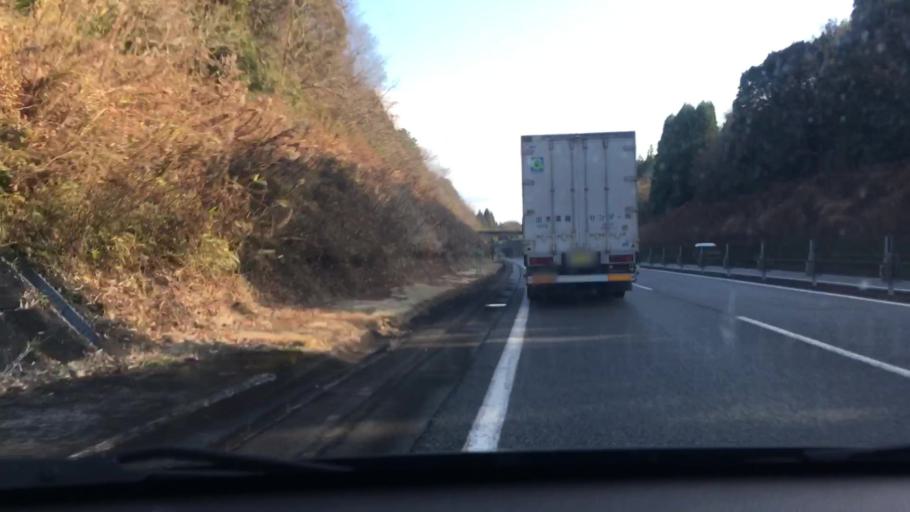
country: JP
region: Kagoshima
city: Okuchi-shinohara
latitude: 31.9122
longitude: 130.7045
